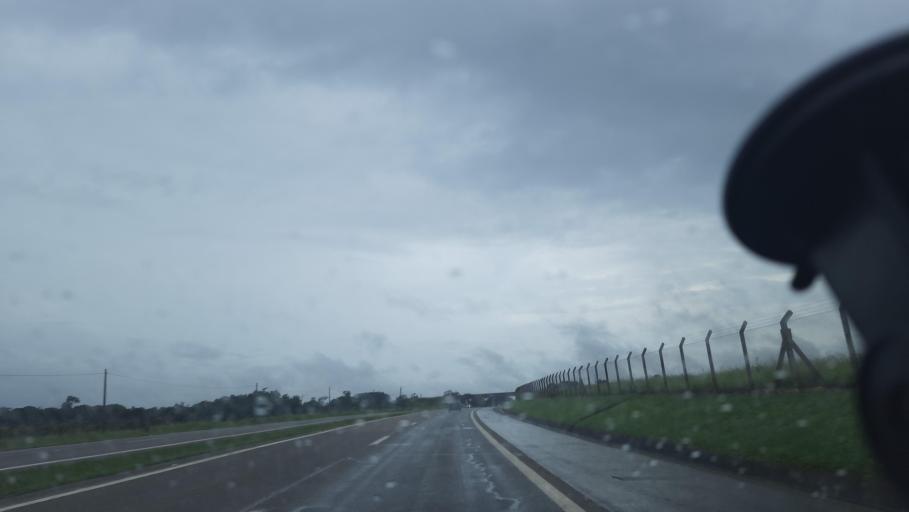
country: BR
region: Sao Paulo
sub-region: Casa Branca
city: Casa Branca
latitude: -21.8040
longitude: -47.0597
